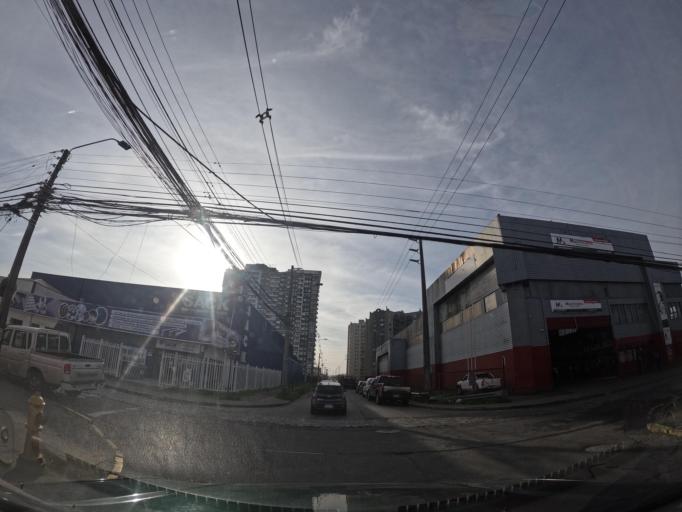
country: CL
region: Biobio
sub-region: Provincia de Concepcion
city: Concepcion
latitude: -36.8188
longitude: -73.0531
